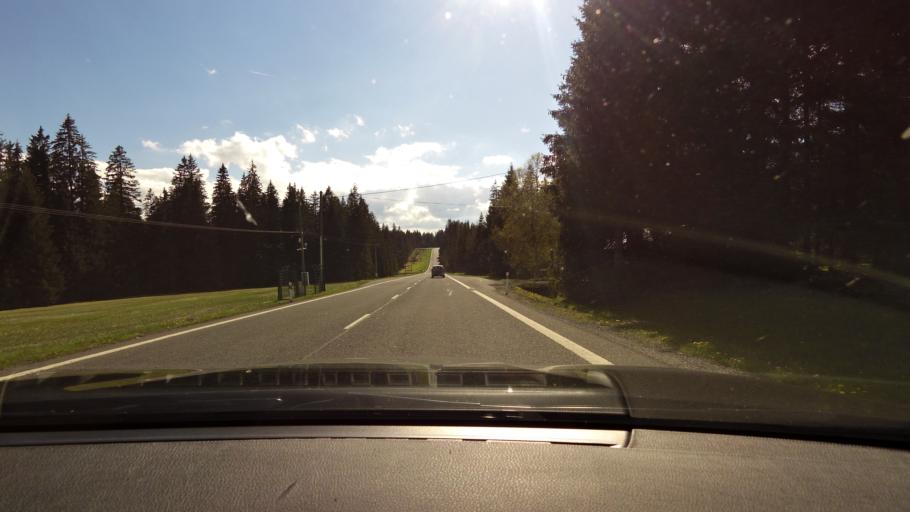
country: CZ
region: Plzensky
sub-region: Okres Klatovy
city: Zelezna Ruda
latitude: 49.1667
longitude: 13.2870
